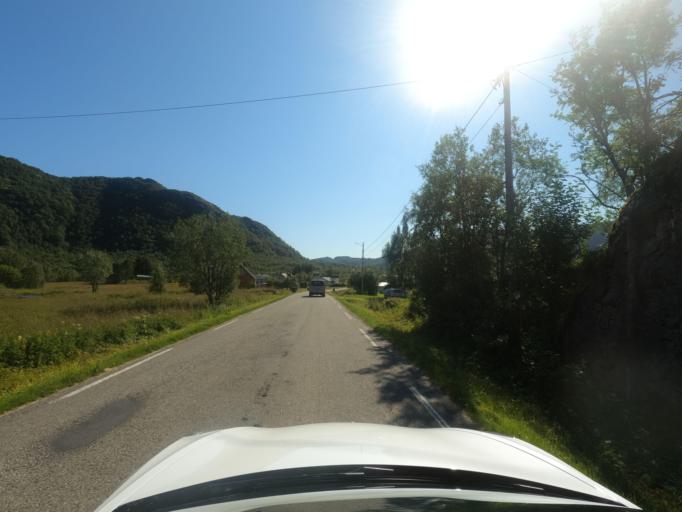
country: NO
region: Nordland
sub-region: Hadsel
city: Stokmarknes
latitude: 68.3101
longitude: 14.9902
